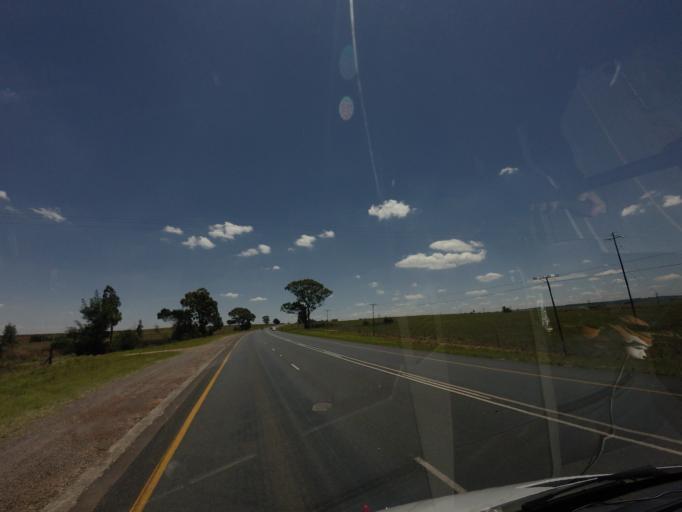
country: ZA
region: Mpumalanga
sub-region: Nkangala District Municipality
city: Belfast
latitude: -25.7327
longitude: 30.1248
